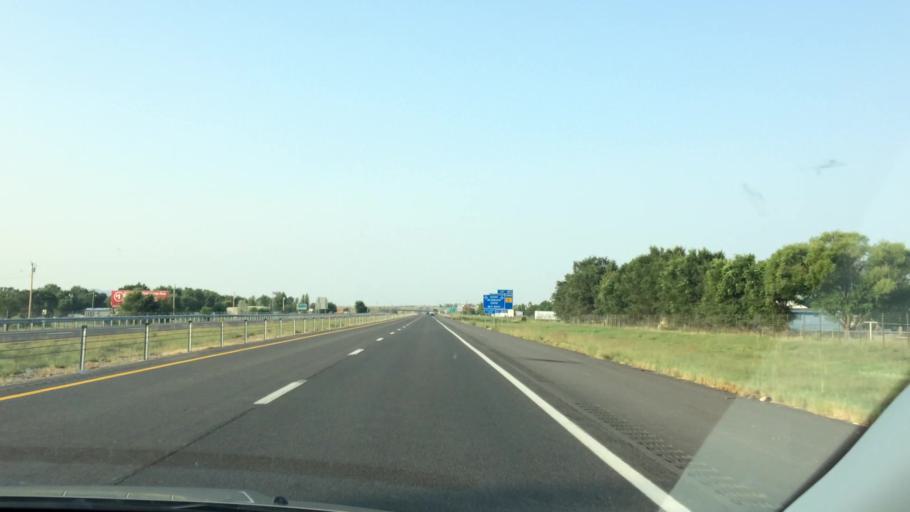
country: US
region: New Mexico
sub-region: Colfax County
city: Raton
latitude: 36.8944
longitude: -104.4274
